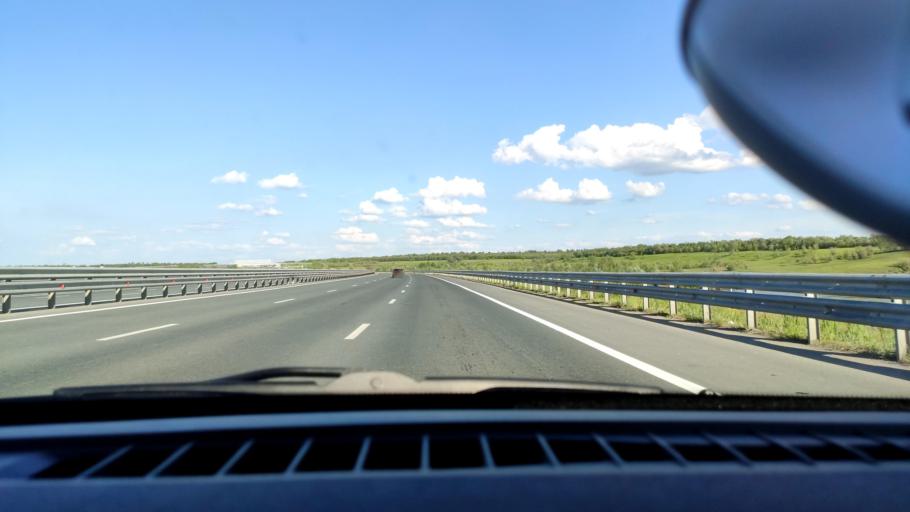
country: RU
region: Samara
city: Smyshlyayevka
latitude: 53.1512
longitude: 50.3570
